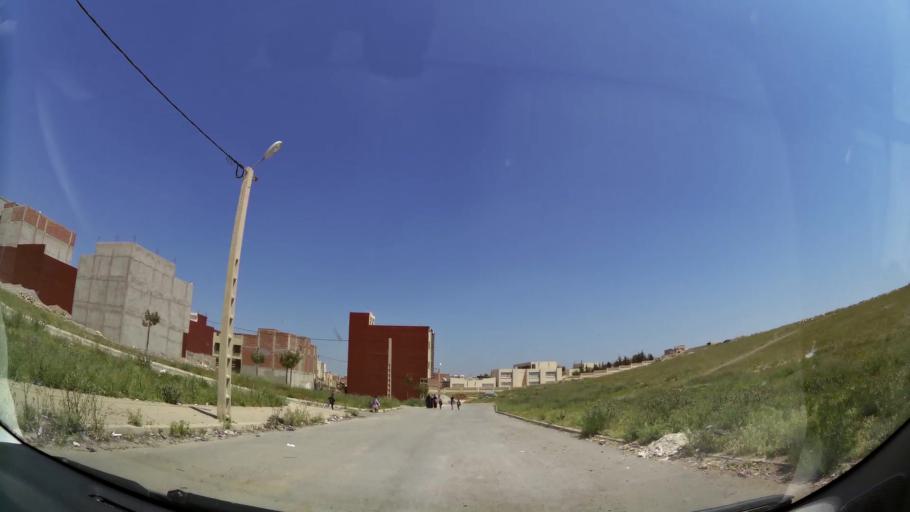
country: MA
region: Oriental
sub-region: Oujda-Angad
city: Oujda
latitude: 34.6773
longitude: -1.9509
